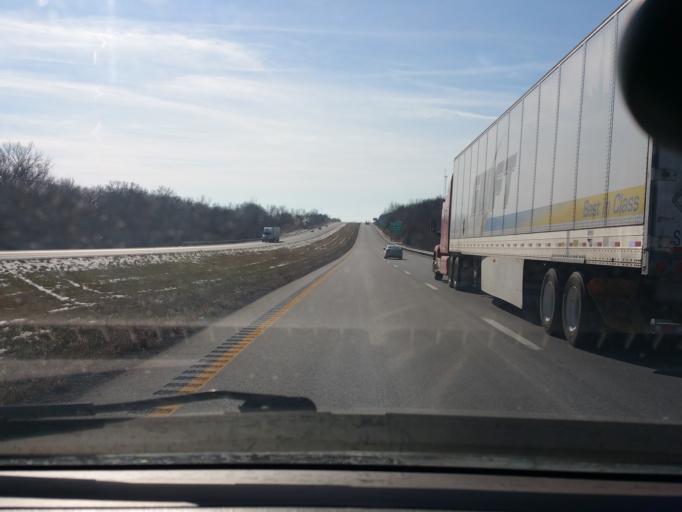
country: US
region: Missouri
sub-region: Clinton County
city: Cameron
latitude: 39.7728
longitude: -94.2127
